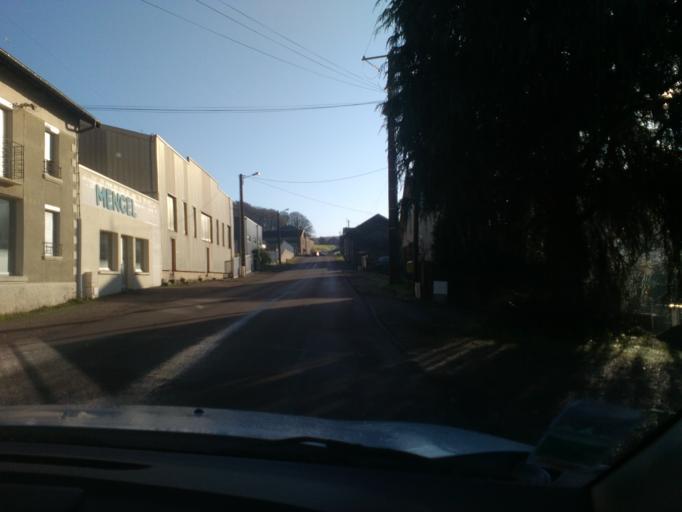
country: FR
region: Lorraine
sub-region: Departement des Vosges
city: Xertigny
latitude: 48.0510
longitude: 6.3777
